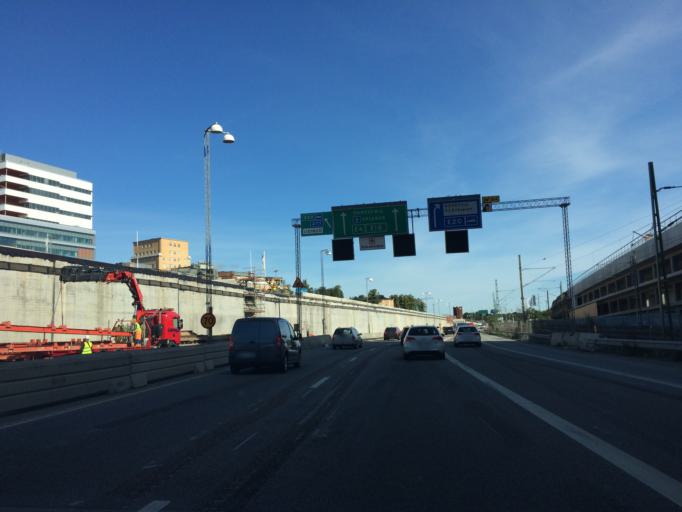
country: SE
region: Stockholm
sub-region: Norrtalje Kommun
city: Bergshamra
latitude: 59.3471
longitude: 18.0325
